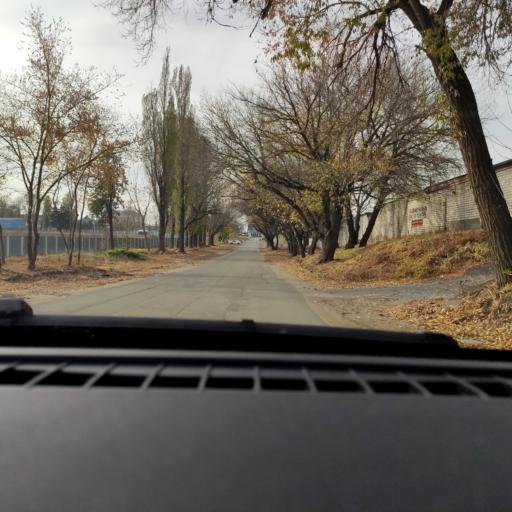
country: RU
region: Voronezj
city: Voronezh
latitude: 51.6604
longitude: 39.2880
